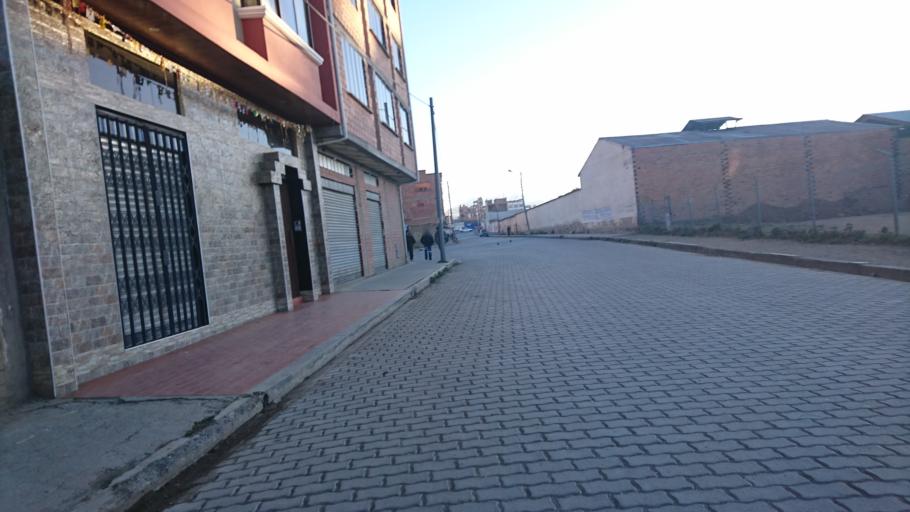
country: BO
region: La Paz
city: La Paz
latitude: -16.4982
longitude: -68.1884
